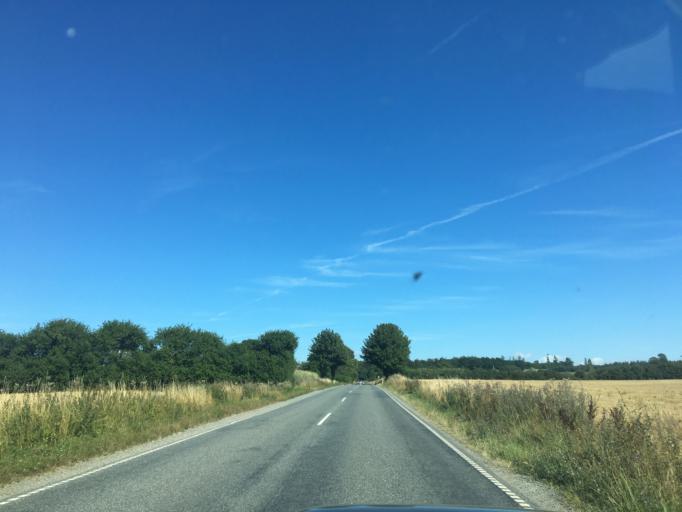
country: DK
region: South Denmark
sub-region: Assens Kommune
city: Arup
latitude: 55.4035
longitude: 9.9938
